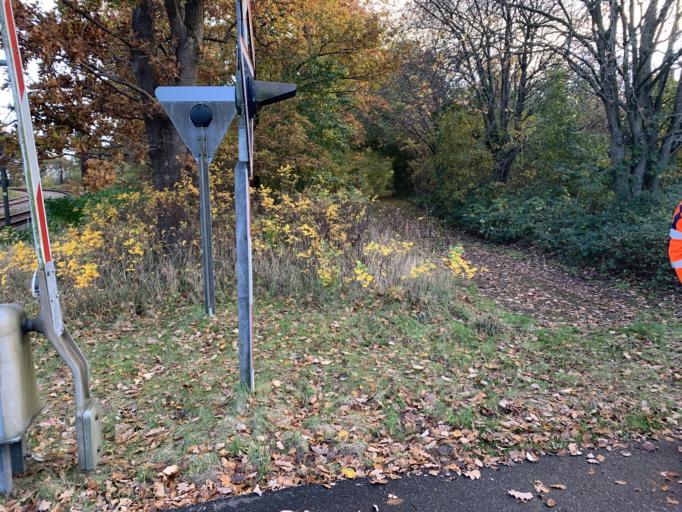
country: DK
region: South Denmark
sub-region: Aabenraa Kommune
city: Tinglev
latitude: 54.9310
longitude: 9.2565
